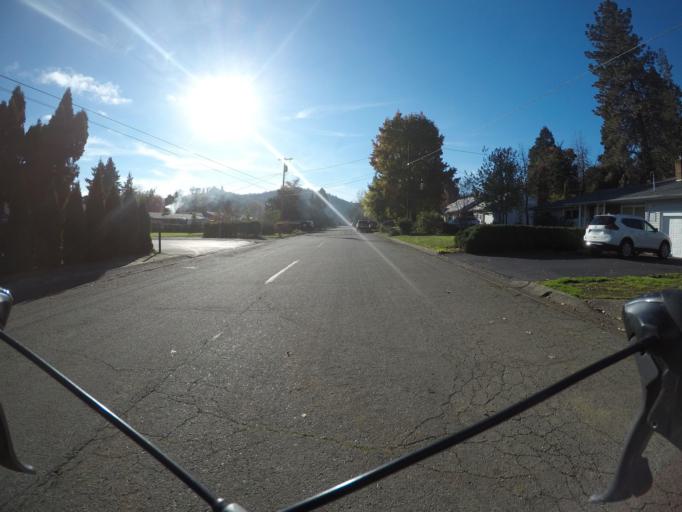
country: US
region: Oregon
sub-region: Douglas County
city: Roseburg
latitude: 43.2023
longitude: -123.3581
